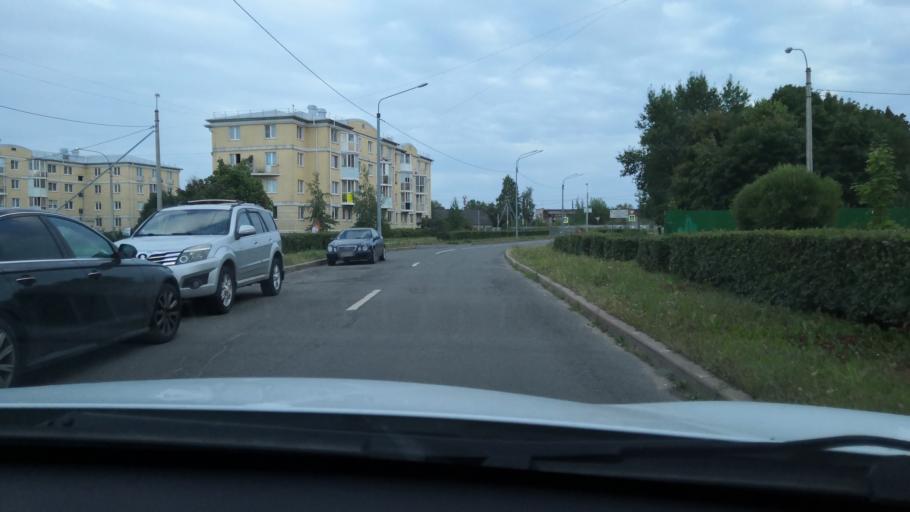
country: RU
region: St.-Petersburg
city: Pushkin
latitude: 59.7017
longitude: 30.3883
